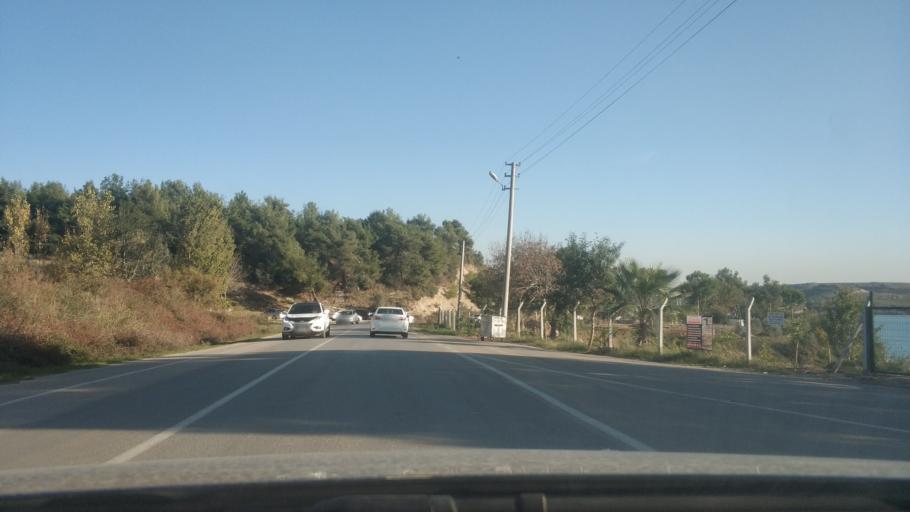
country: TR
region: Adana
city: Adana
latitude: 37.1054
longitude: 35.2977
